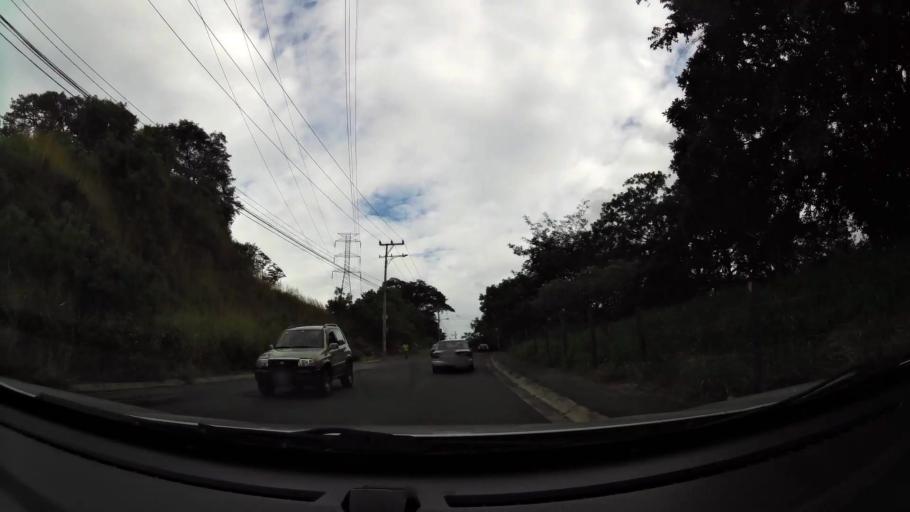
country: CR
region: Heredia
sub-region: Canton de Belen
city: San Antonio
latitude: 9.9657
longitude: -84.1868
